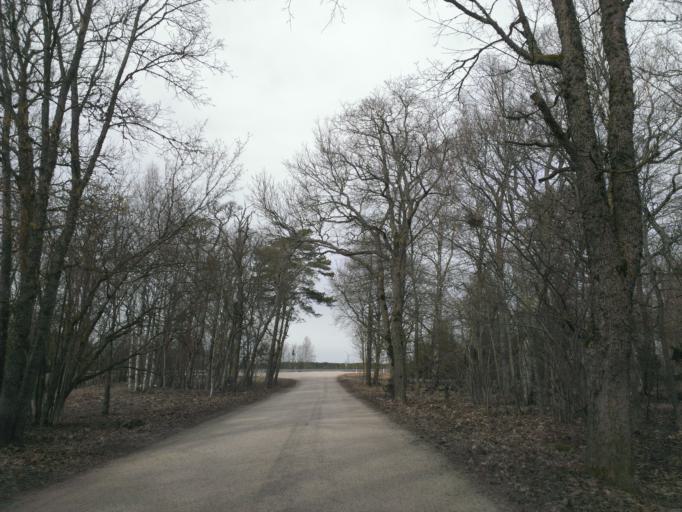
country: EE
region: Laeaene
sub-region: Lihula vald
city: Lihula
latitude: 58.5891
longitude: 23.5374
